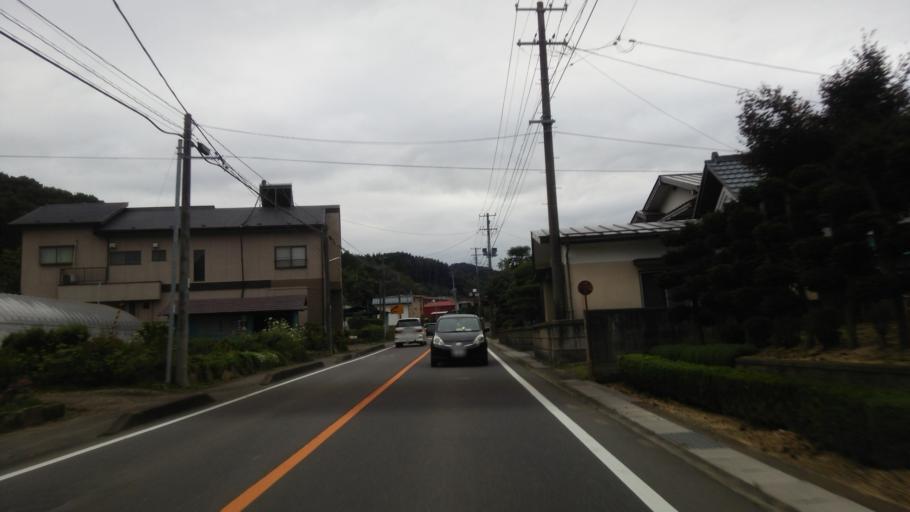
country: JP
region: Fukushima
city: Sukagawa
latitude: 37.1853
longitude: 140.2219
